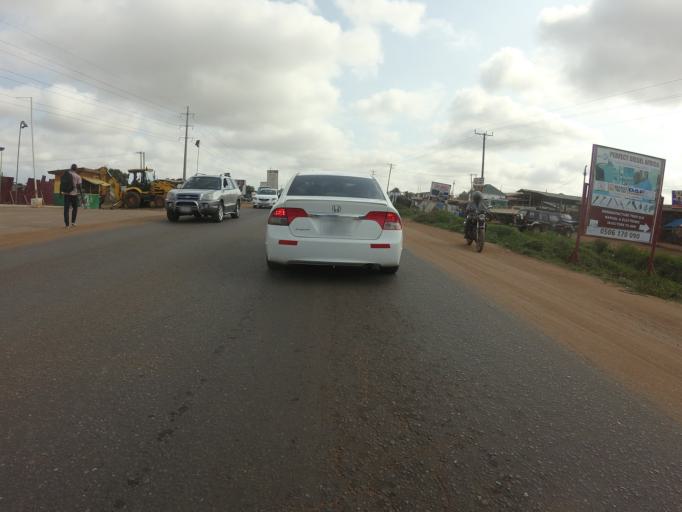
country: GH
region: Greater Accra
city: Tema
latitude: 5.7432
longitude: -0.0128
